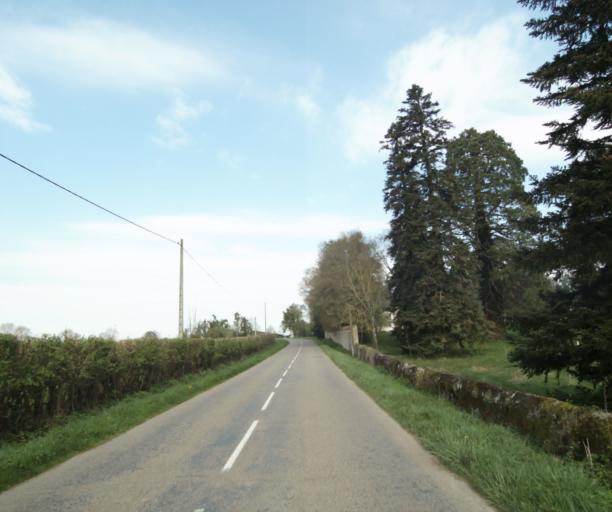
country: FR
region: Bourgogne
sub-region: Departement de Saone-et-Loire
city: Palinges
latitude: 46.5015
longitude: 4.2102
